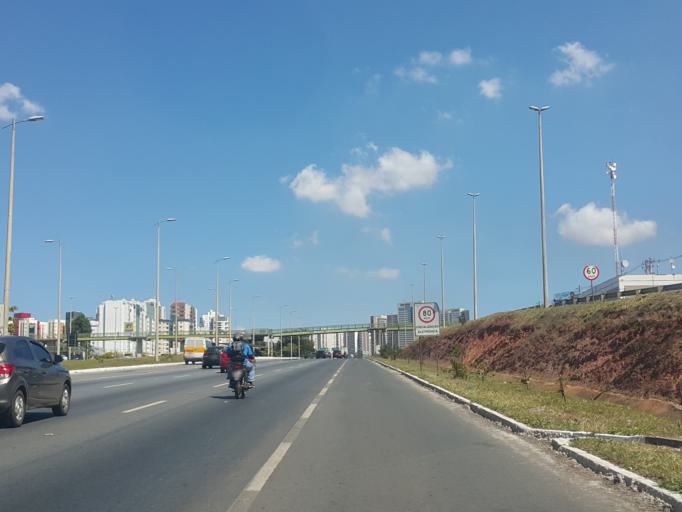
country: BR
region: Federal District
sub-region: Brasilia
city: Brasilia
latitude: -15.8256
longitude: -48.0285
